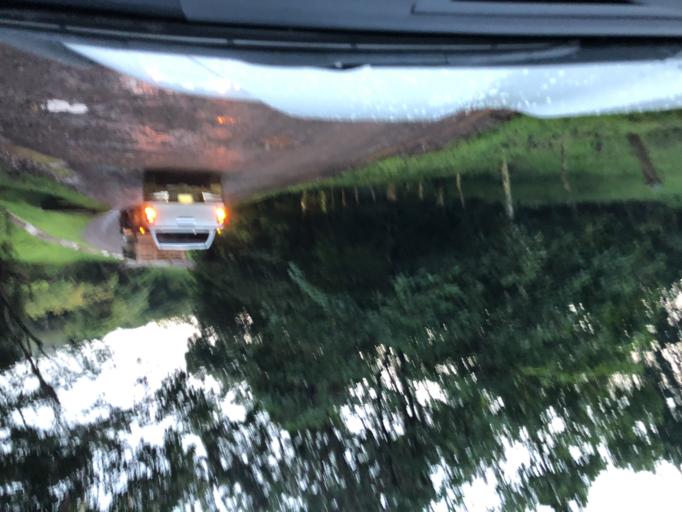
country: NI
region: Chontales
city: La Libertad
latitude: 12.1580
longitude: -85.1785
